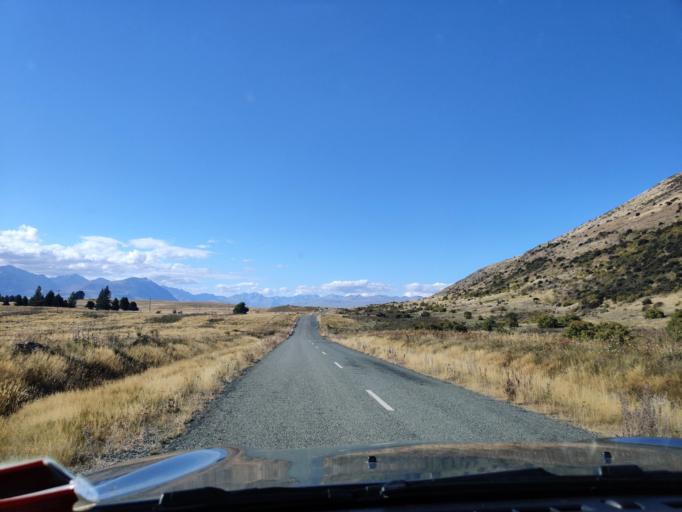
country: NZ
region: Canterbury
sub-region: Timaru District
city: Pleasant Point
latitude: -43.9864
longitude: 170.4555
